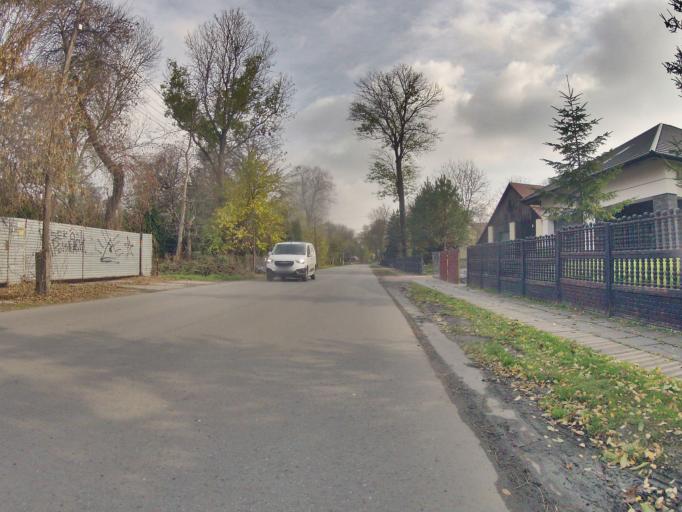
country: PL
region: Lesser Poland Voivodeship
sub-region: Powiat wielicki
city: Wegrzce Wielkie
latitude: 50.0698
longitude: 20.1062
